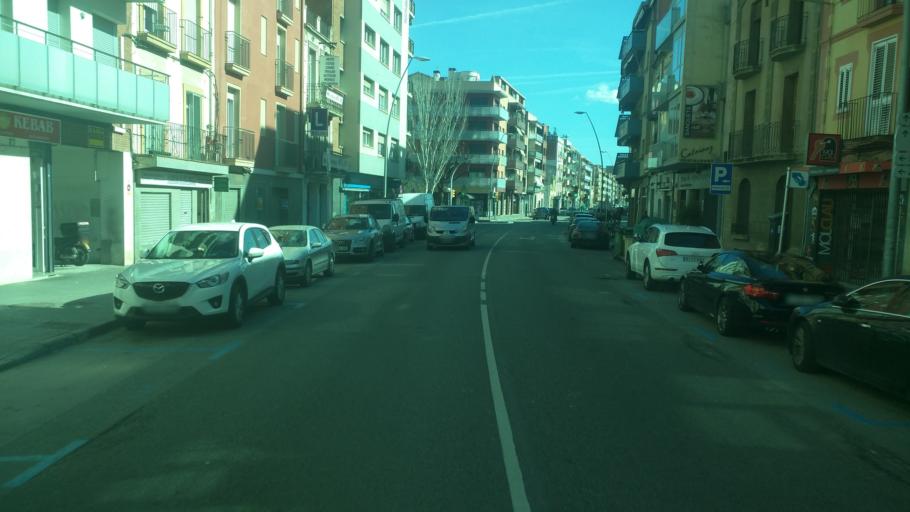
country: ES
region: Catalonia
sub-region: Provincia de Barcelona
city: Molins de Rei
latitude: 41.4094
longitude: 2.0201
